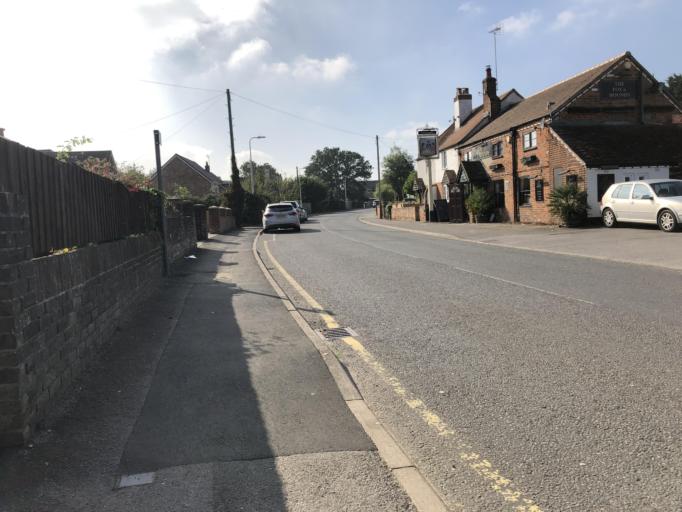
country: GB
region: England
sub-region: West Berkshire
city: Tilehurst
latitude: 51.4522
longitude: -1.0537
